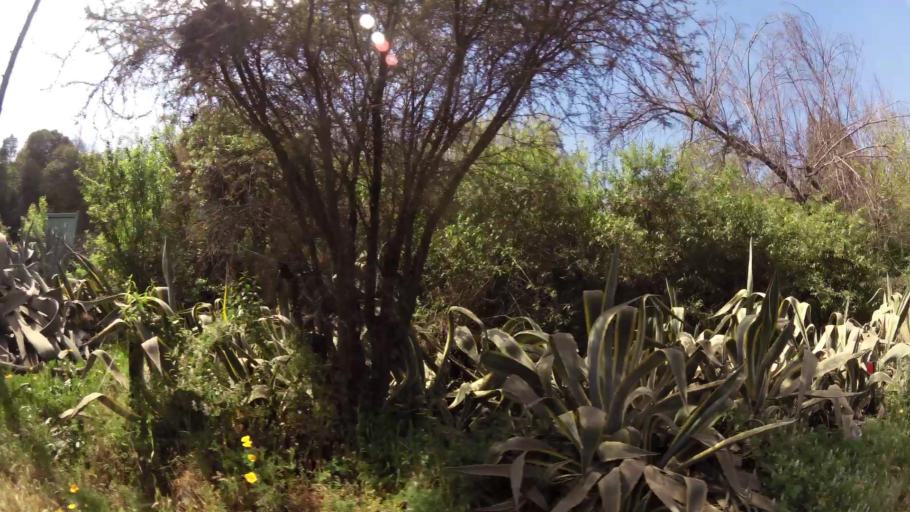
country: CL
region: Santiago Metropolitan
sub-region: Provincia de Santiago
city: Villa Presidente Frei, Nunoa, Santiago, Chile
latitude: -33.4684
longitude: -70.5235
